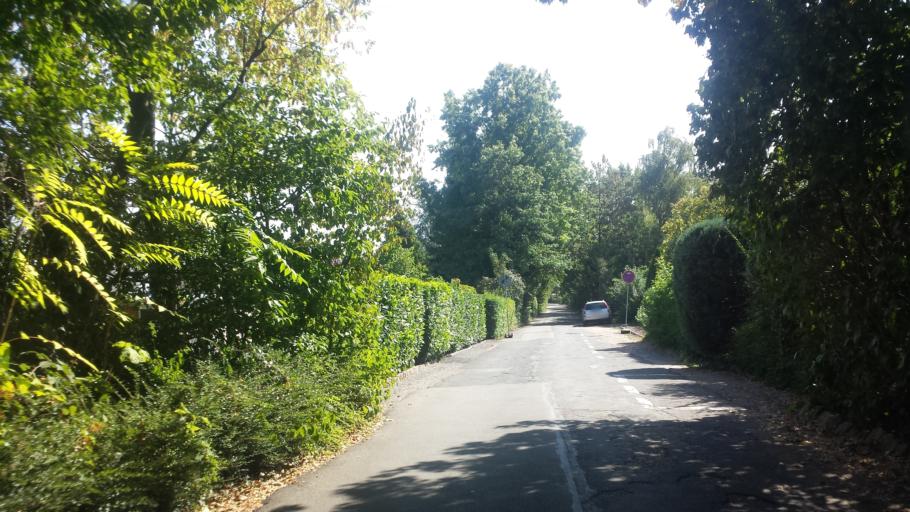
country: DE
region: Rheinland-Pfalz
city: Lachen-Speyerdorf
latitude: 49.3522
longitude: 8.1761
